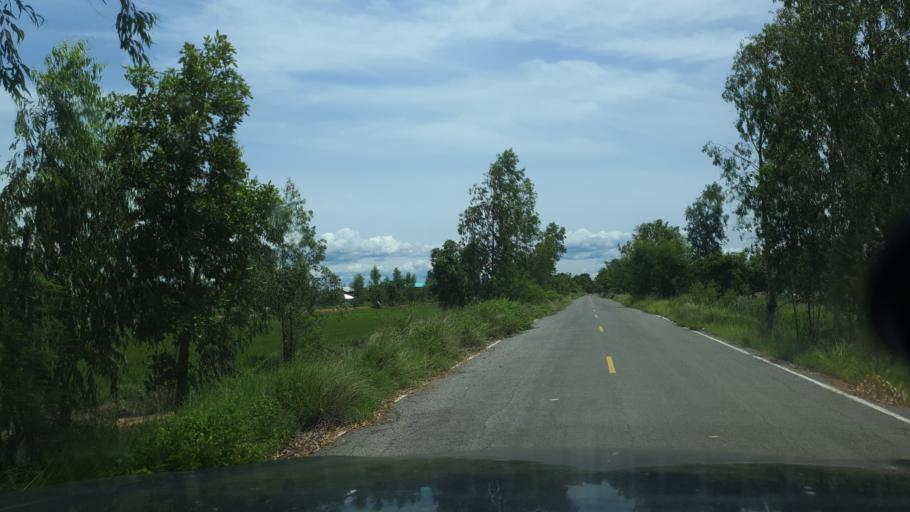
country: TH
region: Sukhothai
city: Ban Na
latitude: 17.1031
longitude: 99.6789
